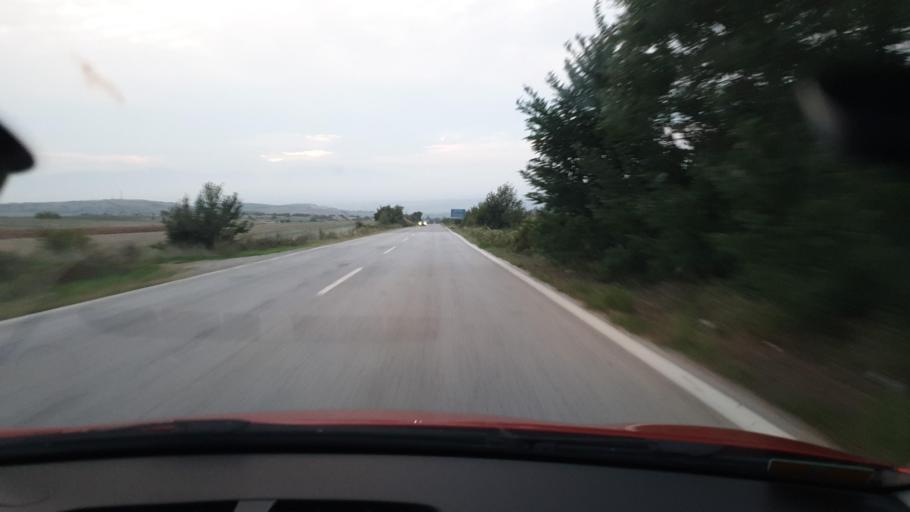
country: GR
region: Central Macedonia
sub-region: Nomos Kilkis
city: Polykastro
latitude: 41.0079
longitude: 22.6906
